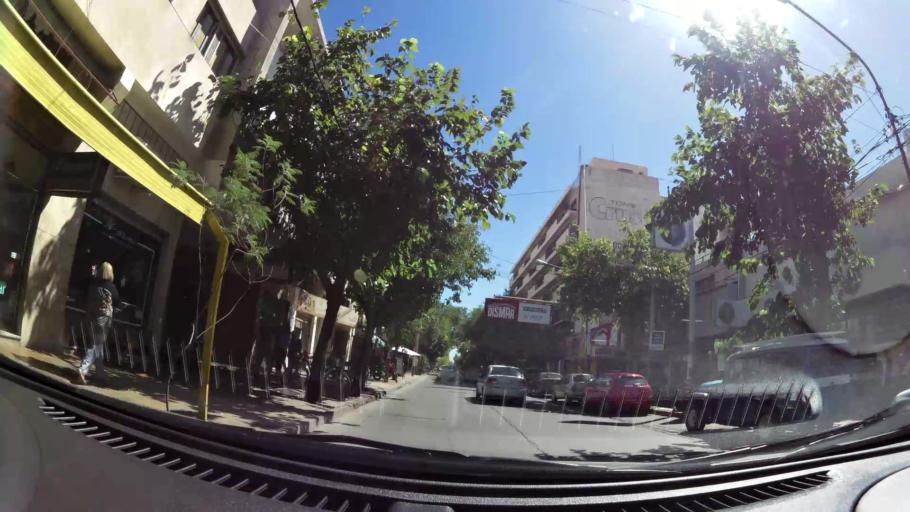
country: AR
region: San Juan
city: San Juan
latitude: -31.5385
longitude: -68.5244
